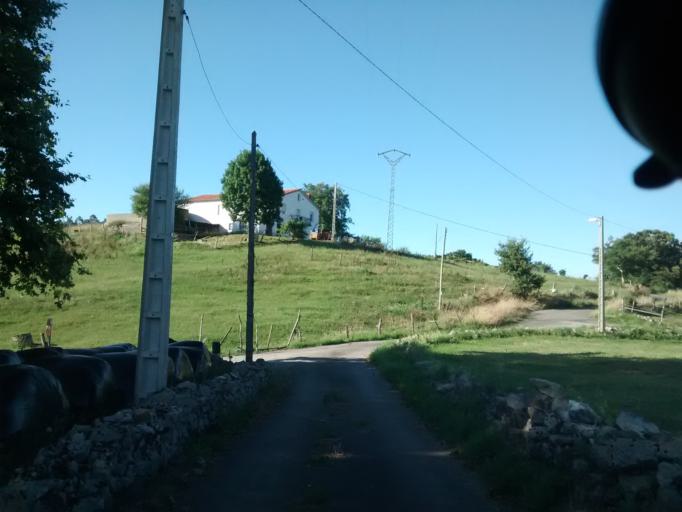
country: ES
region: Cantabria
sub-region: Provincia de Cantabria
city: Entrambasaguas
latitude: 43.3640
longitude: -3.7070
